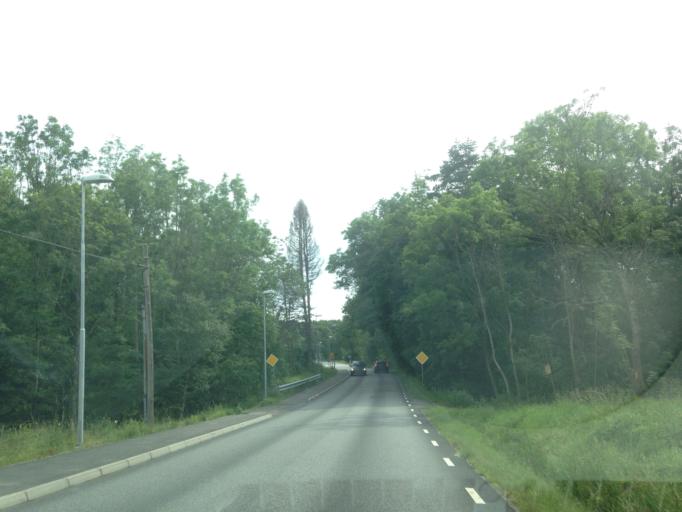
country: SE
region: Vaestra Goetaland
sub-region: Goteborg
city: Goeteborg
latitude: 57.7682
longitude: 11.9499
